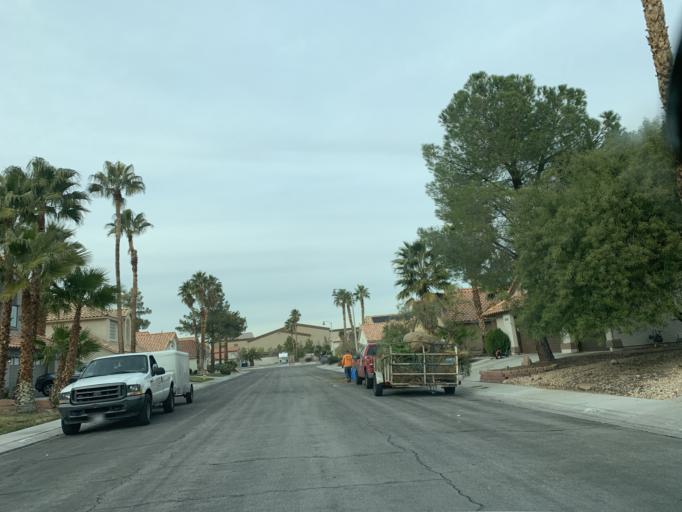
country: US
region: Nevada
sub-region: Clark County
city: Summerlin South
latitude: 36.1416
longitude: -115.2960
